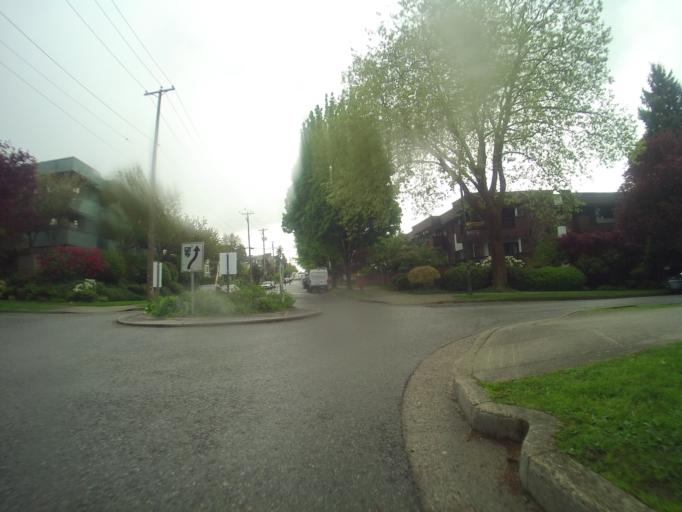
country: CA
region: British Columbia
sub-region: Fraser Valley Regional District
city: North Vancouver
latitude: 49.2733
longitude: -123.0736
